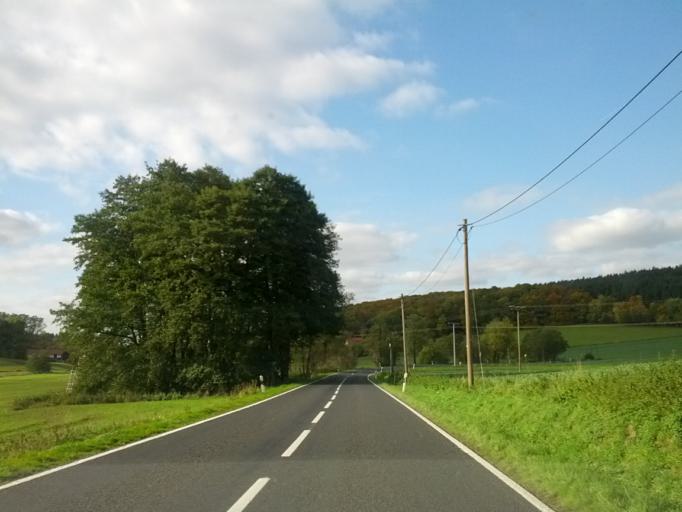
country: DE
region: Thuringia
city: Marksuhl
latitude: 50.9175
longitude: 10.1859
